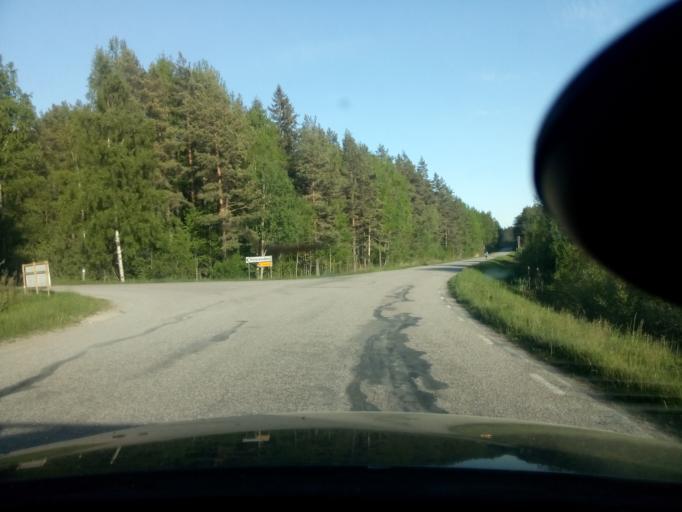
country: SE
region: Soedermanland
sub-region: Nykopings Kommun
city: Nykoping
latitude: 58.7796
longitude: 17.0266
